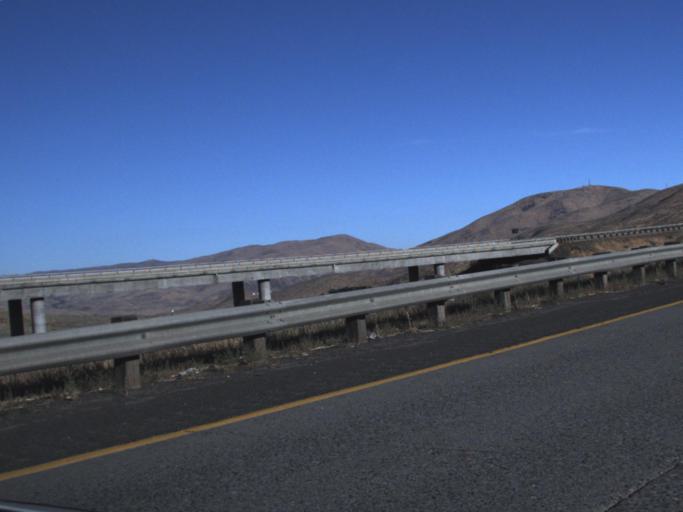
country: US
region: Washington
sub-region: Yakima County
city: Terrace Heights
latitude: 46.7472
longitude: -120.3889
